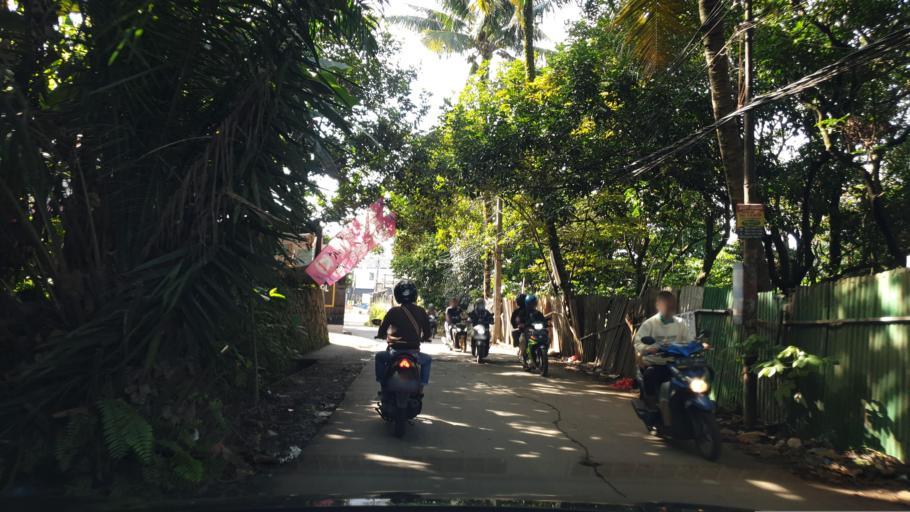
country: ID
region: West Java
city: Sawangan
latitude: -6.3705
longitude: 106.7845
